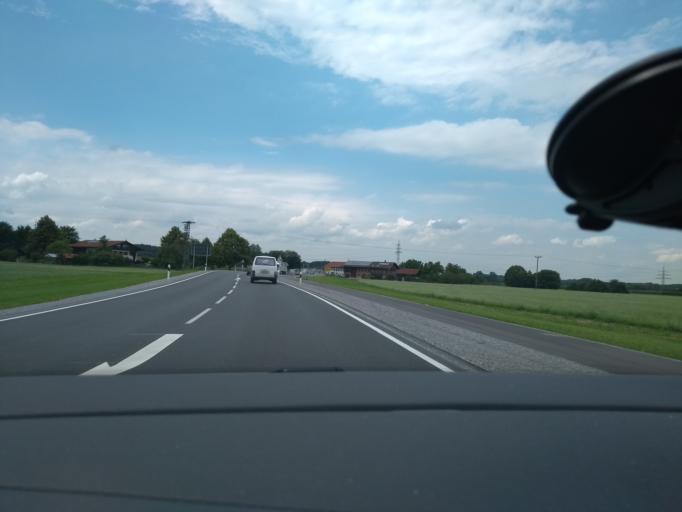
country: DE
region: Bavaria
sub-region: Upper Bavaria
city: Rosenheim
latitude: 47.8844
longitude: 12.1153
